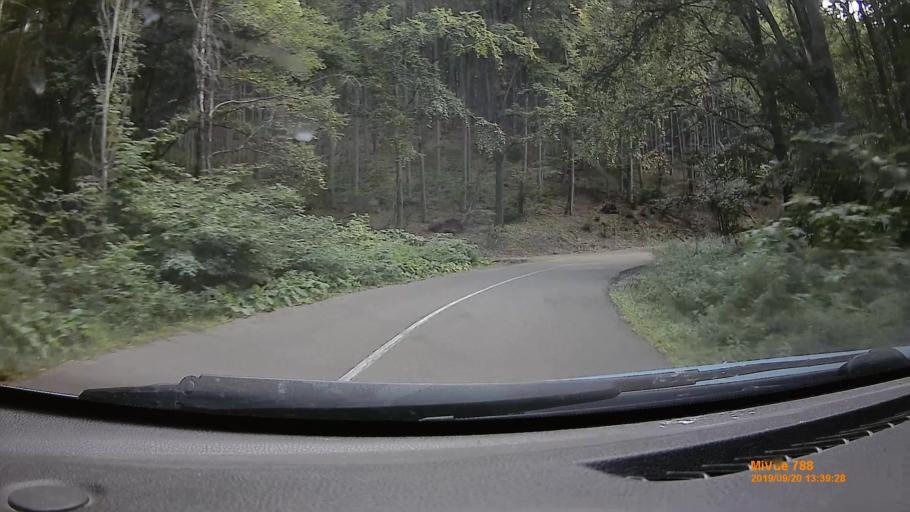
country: HU
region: Heves
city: Szilvasvarad
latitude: 48.0580
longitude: 20.5309
